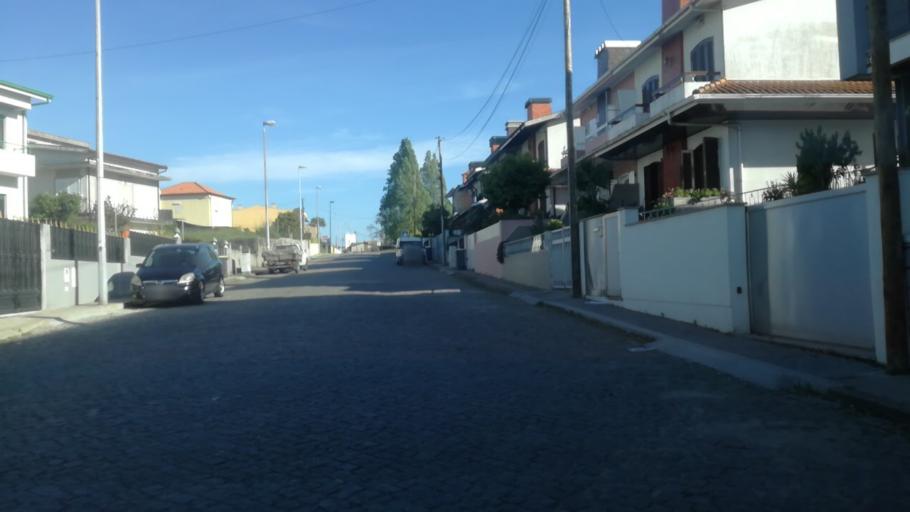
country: PT
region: Porto
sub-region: Maia
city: Gemunde
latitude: 41.2520
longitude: -8.6678
